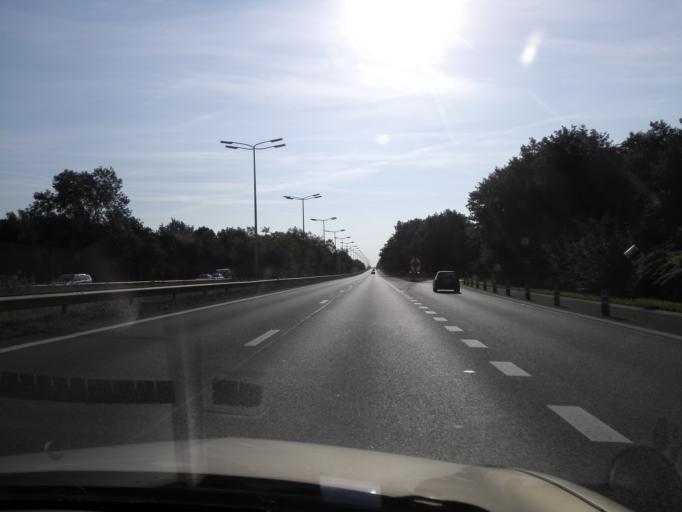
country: BE
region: Flanders
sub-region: Provincie Limburg
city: Zonhoven
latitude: 51.0119
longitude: 5.3280
